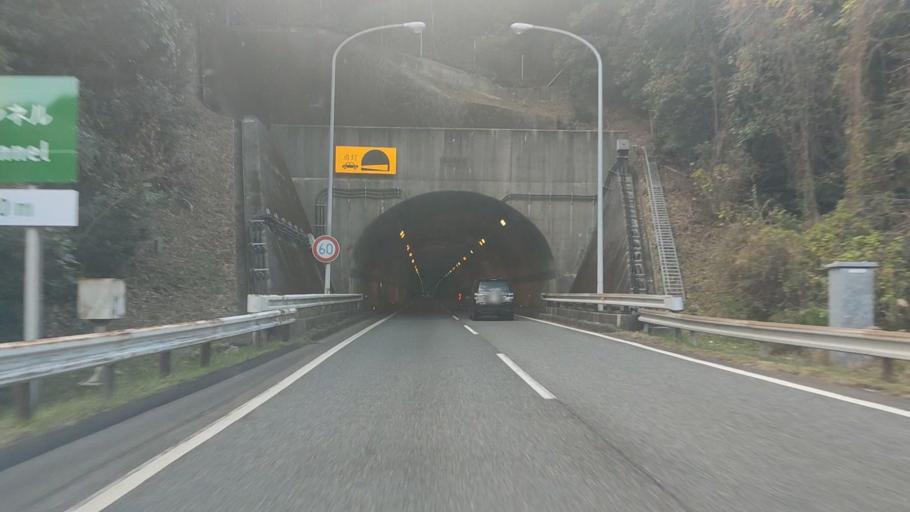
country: JP
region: Yamaguchi
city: Shimonoseki
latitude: 33.9206
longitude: 130.9685
